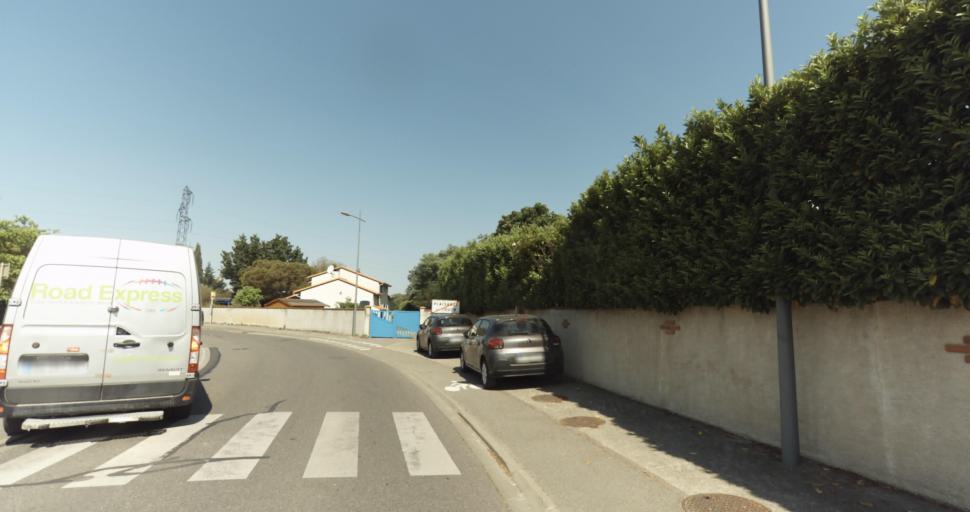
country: FR
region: Midi-Pyrenees
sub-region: Departement de la Haute-Garonne
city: La Salvetat-Saint-Gilles
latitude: 43.5832
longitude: 1.2789
